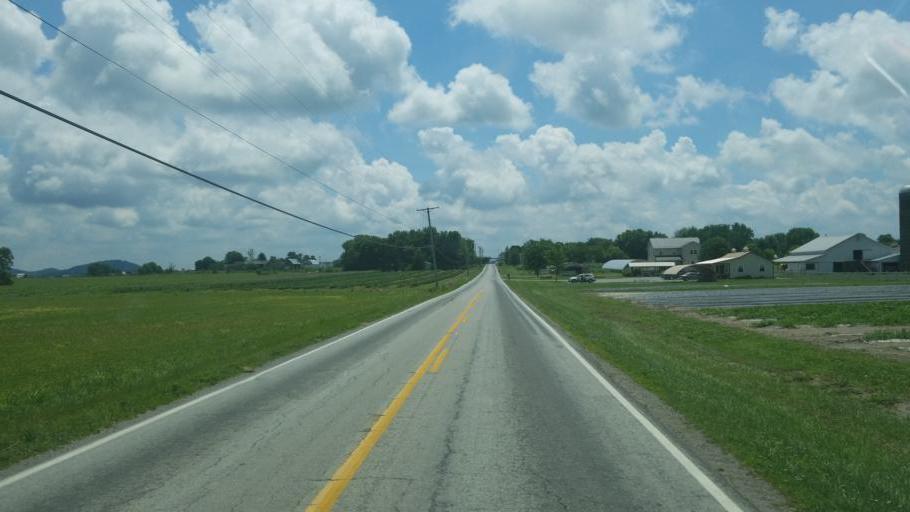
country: US
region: Ohio
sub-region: Highland County
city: Greenfield
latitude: 39.2250
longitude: -83.4241
